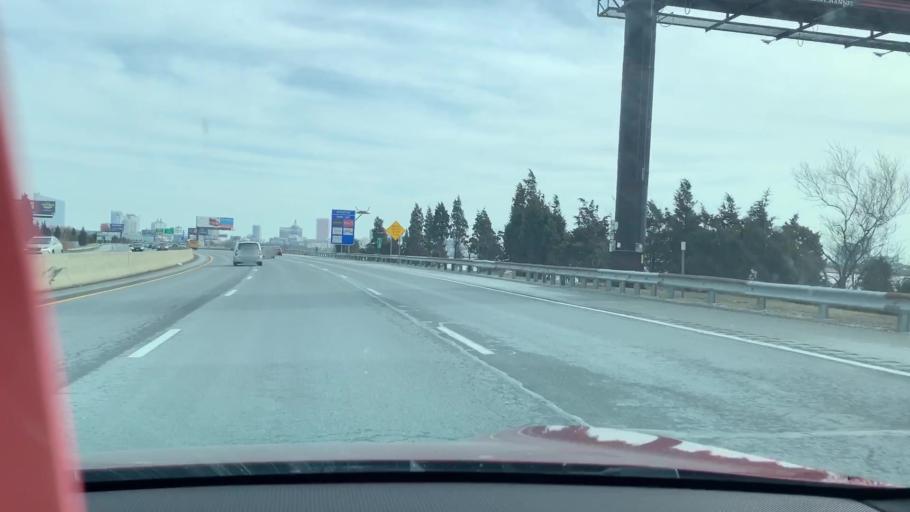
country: US
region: New Jersey
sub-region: Atlantic County
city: Ventnor City
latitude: 39.3678
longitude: -74.4619
